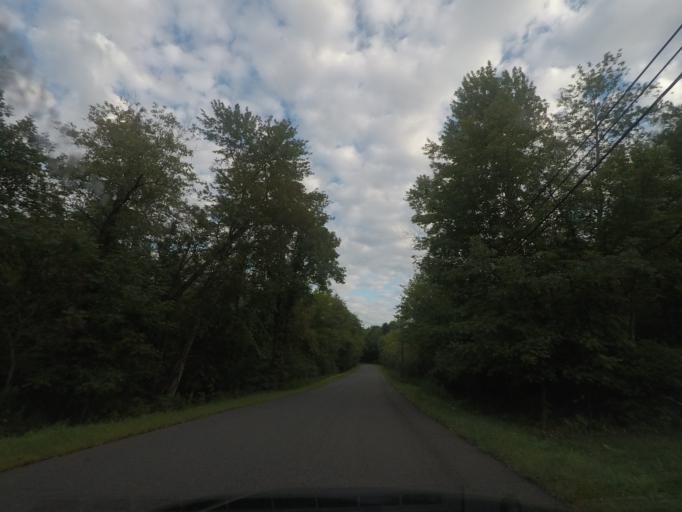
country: US
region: New York
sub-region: Rensselaer County
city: Nassau
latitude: 42.4902
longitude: -73.5988
